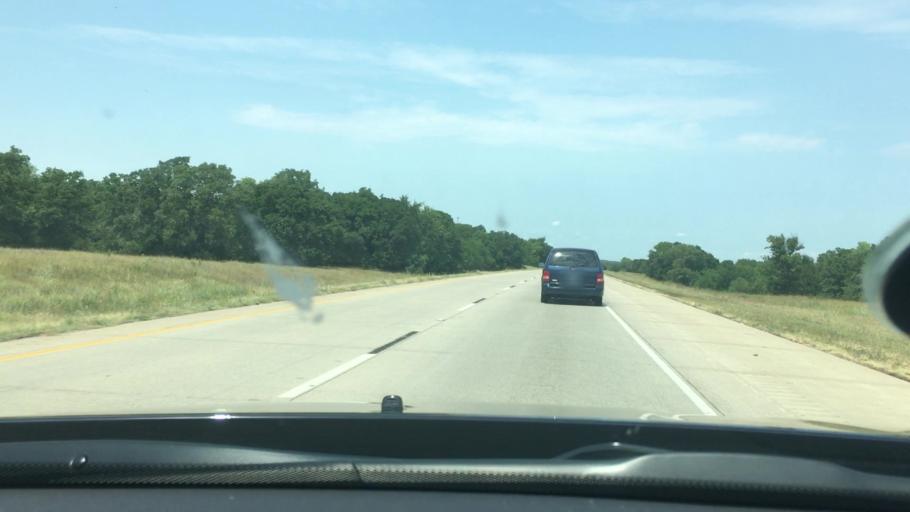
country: US
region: Oklahoma
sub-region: Love County
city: Marietta
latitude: 33.9971
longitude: -97.1403
